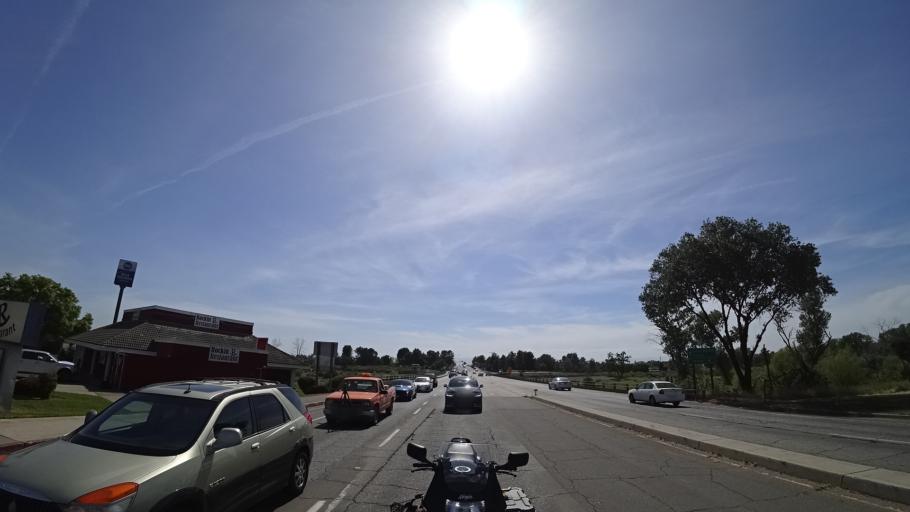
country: US
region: California
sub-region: Tehama County
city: Red Bluff
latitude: 40.1826
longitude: -122.2206
